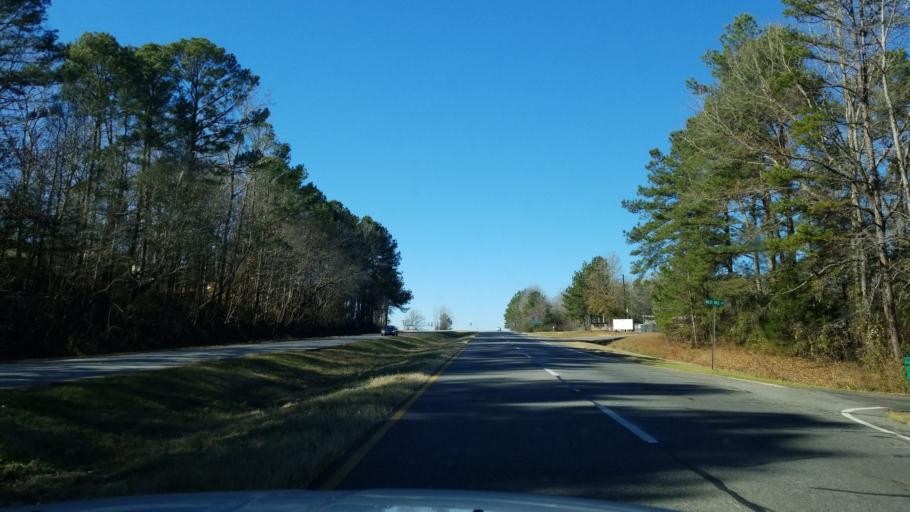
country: US
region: Alabama
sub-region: Tuscaloosa County
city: Northport
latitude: 33.2504
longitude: -87.6833
